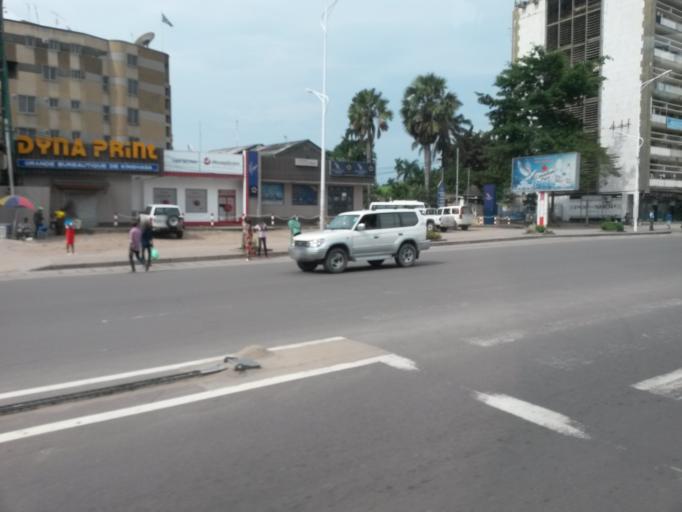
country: CD
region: Kinshasa
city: Kinshasa
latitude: -4.3055
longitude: 15.3031
